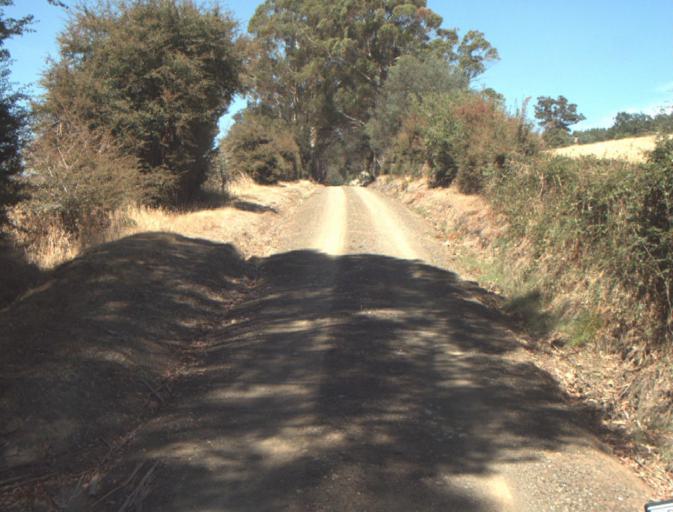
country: AU
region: Tasmania
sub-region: Launceston
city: Mayfield
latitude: -41.2459
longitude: 147.1215
